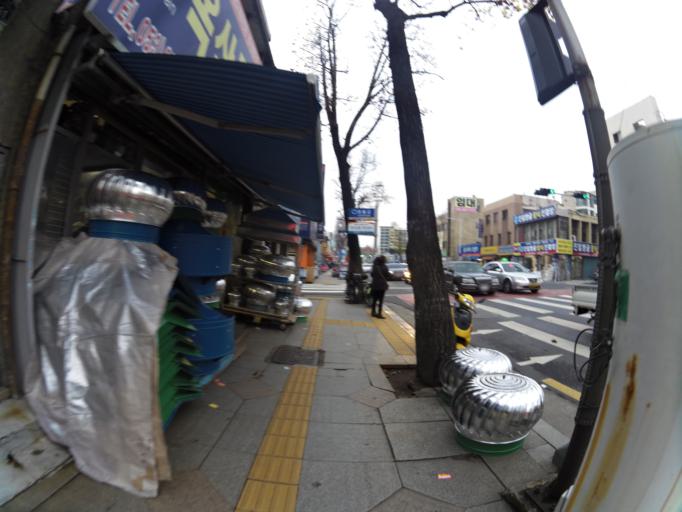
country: KR
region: Daegu
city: Daegu
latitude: 35.8722
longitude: 128.5873
